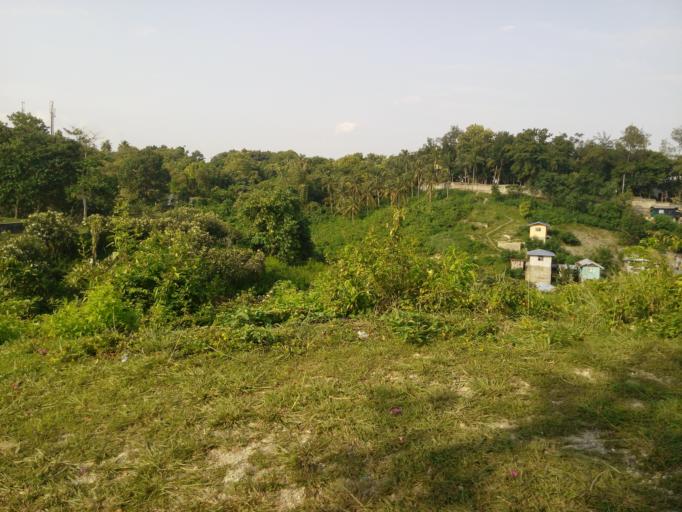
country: PH
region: Central Visayas
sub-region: Cebu City
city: Calero
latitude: 10.3146
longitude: 123.8679
